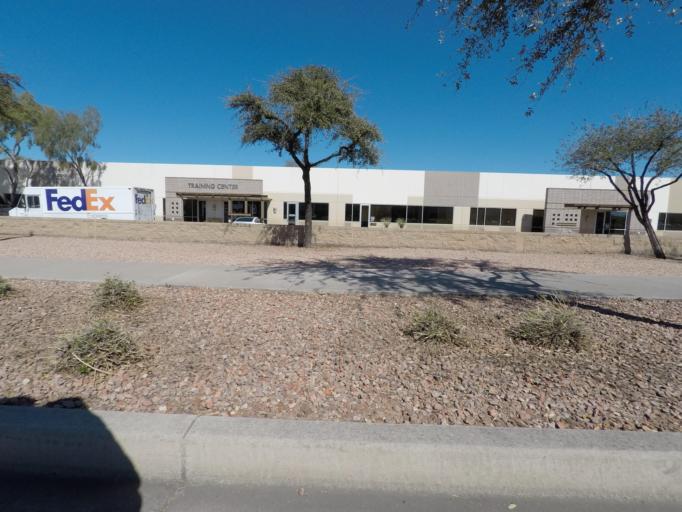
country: US
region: Arizona
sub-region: Maricopa County
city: Guadalupe
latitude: 33.4032
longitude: -111.9921
